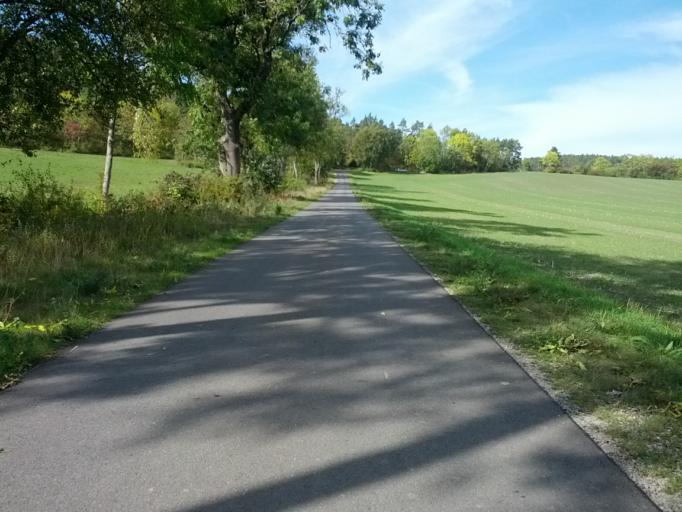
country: DE
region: Thuringia
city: Krauthausen
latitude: 51.0267
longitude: 10.2898
